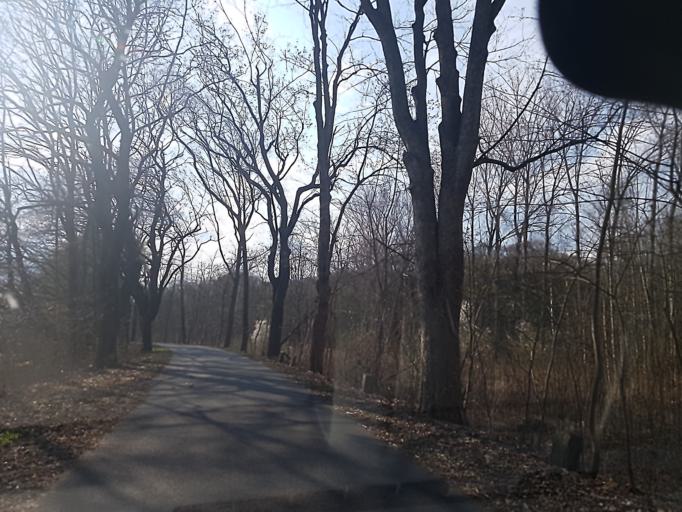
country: DE
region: Brandenburg
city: Doberlug-Kirchhain
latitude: 51.6105
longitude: 13.5353
